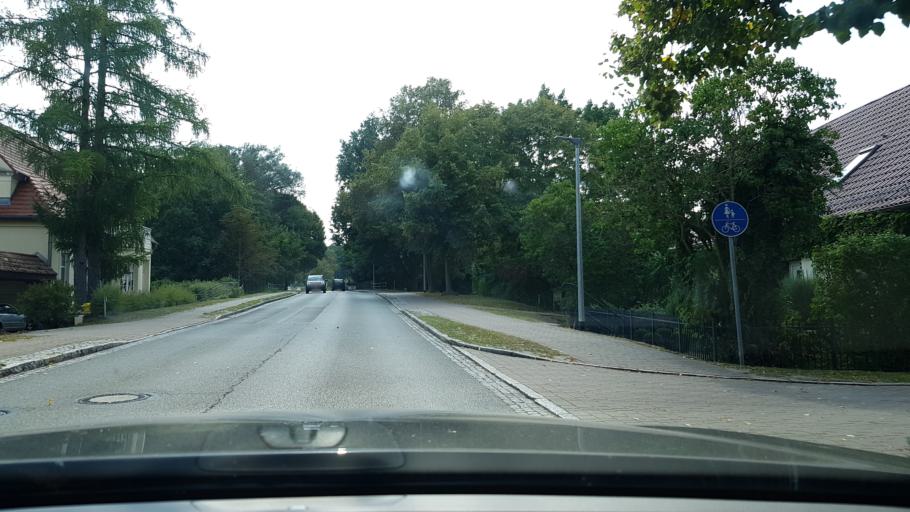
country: DE
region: Brandenburg
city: Lindow
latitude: 52.9662
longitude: 12.9847
